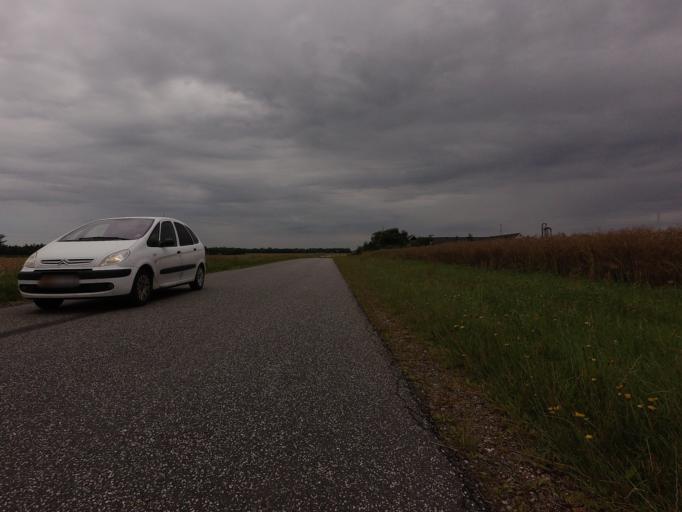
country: DK
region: North Denmark
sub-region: Alborg Kommune
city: Vadum
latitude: 57.1286
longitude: 9.8544
